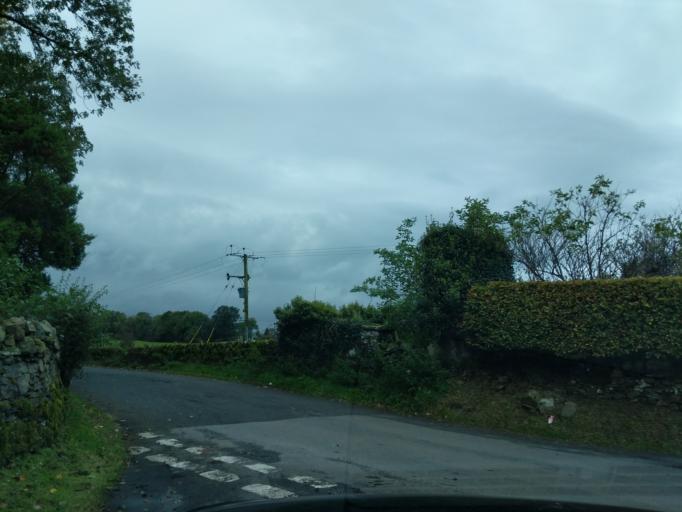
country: GB
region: Scotland
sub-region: Dumfries and Galloway
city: Castle Douglas
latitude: 54.9275
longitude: -3.9407
